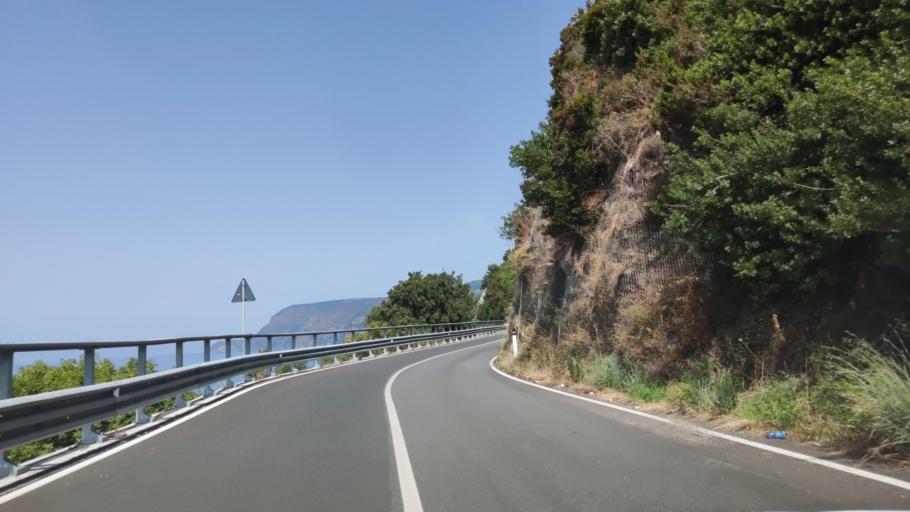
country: IT
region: Calabria
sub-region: Provincia di Reggio Calabria
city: Bagnara Calabra
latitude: 38.2729
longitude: 15.7829
